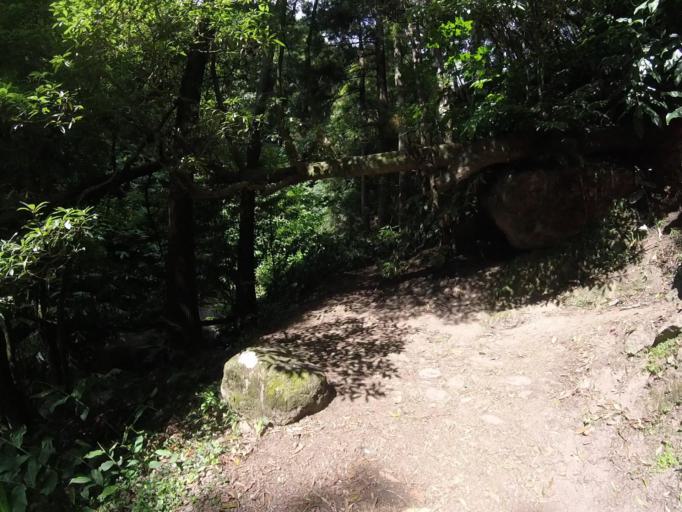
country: PT
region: Azores
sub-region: Povoacao
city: Furnas
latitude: 37.7572
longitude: -25.2017
